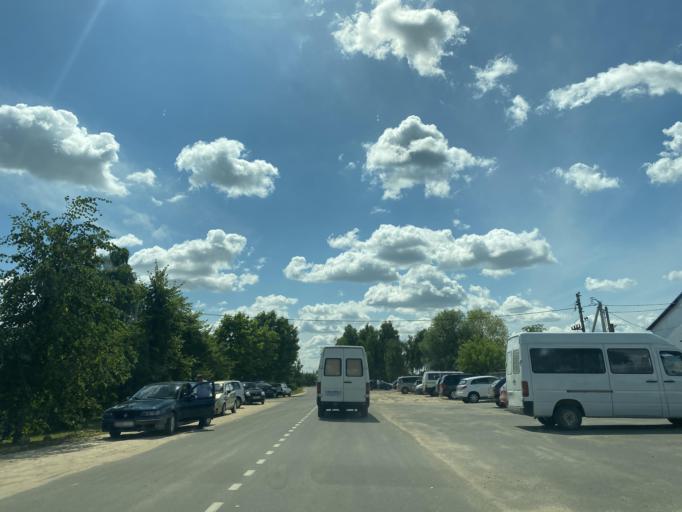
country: BY
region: Brest
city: Ivanava
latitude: 52.1466
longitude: 25.5464
